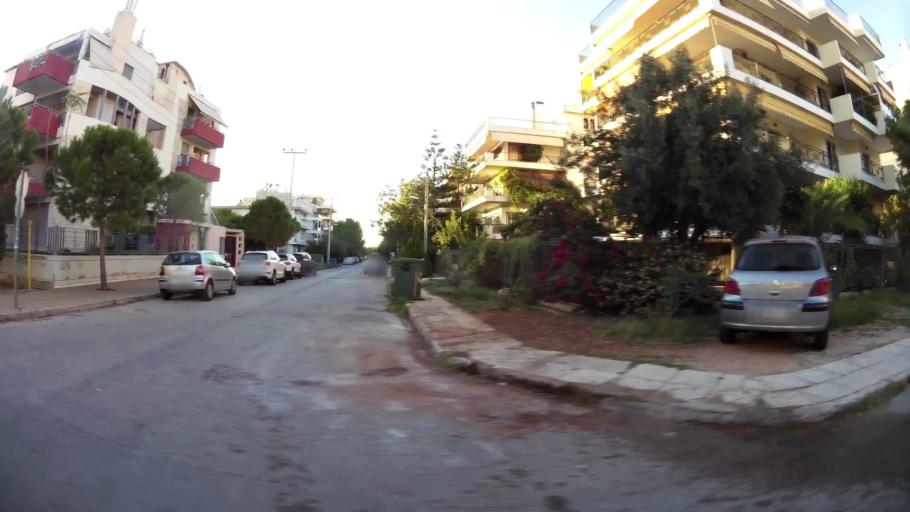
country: GR
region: Attica
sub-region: Nomarchia Athinas
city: Glyfada
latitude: 37.8748
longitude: 23.7512
